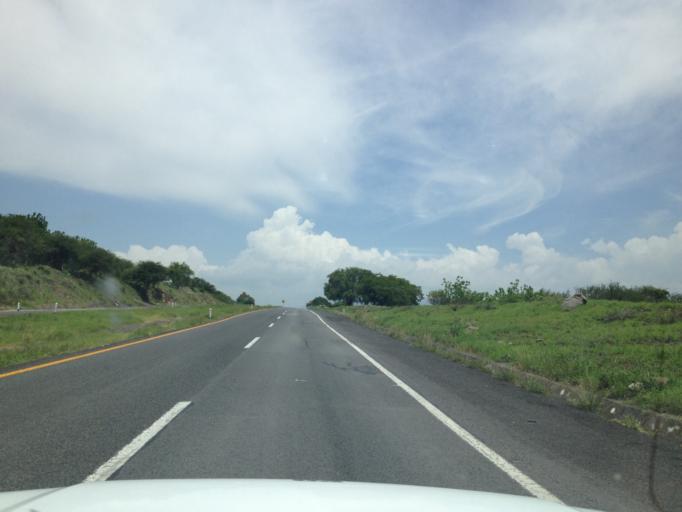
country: MX
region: Michoacan
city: Copandaro de Galeana
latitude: 19.9009
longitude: -101.2646
